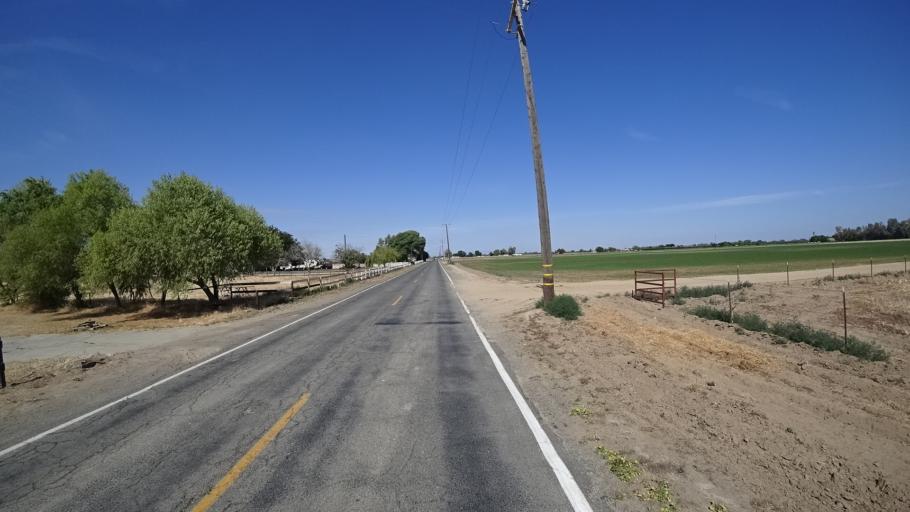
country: US
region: California
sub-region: Kings County
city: Lemoore
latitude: 36.2548
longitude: -119.7558
